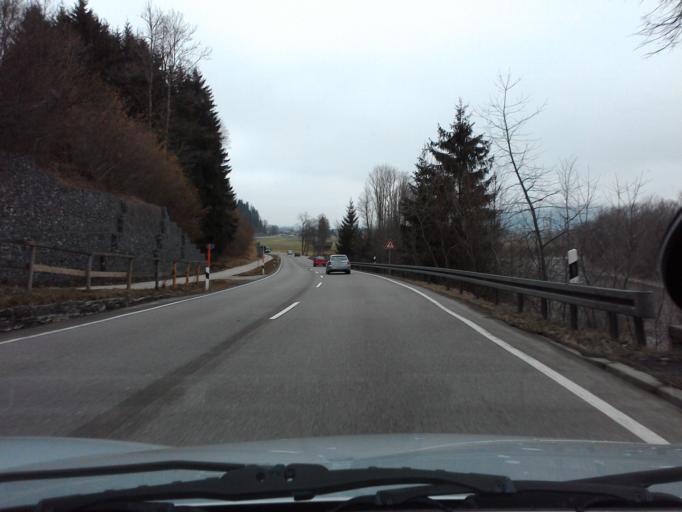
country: DE
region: Bavaria
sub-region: Swabia
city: Sonthofen
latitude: 47.4921
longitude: 10.2666
